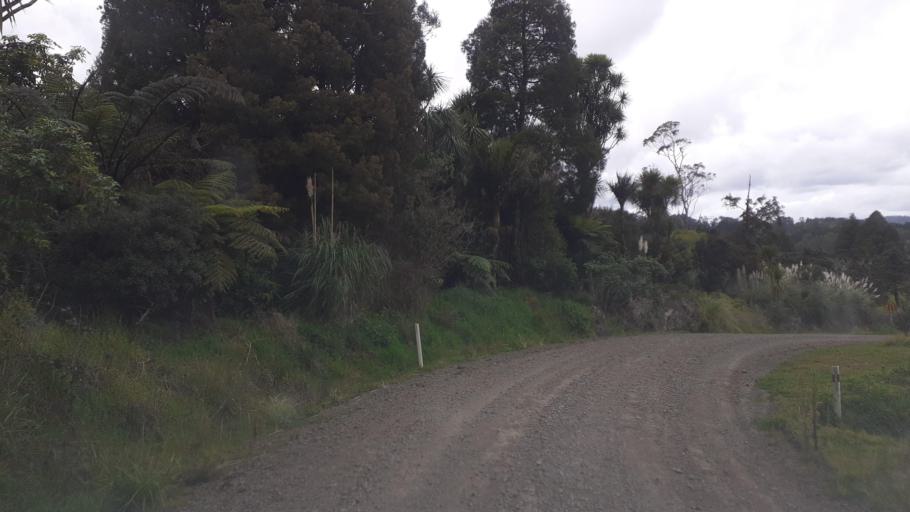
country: NZ
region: Northland
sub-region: Far North District
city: Kaitaia
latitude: -35.5312
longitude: 173.4348
